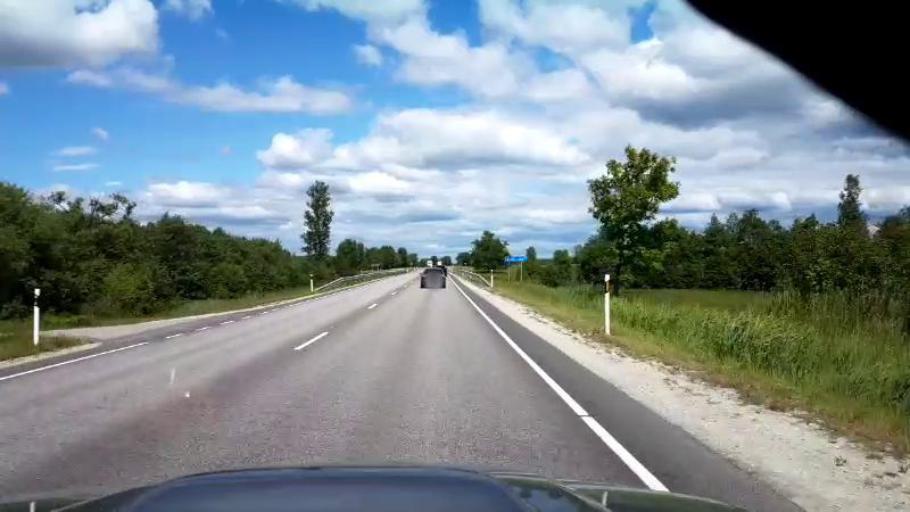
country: EE
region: Paernumaa
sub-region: Sauga vald
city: Sauga
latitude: 58.4931
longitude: 24.5317
